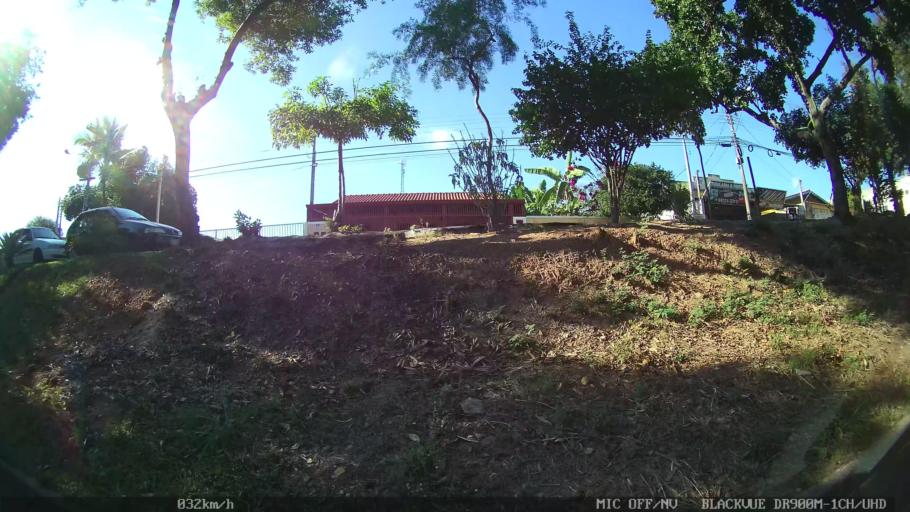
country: BR
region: Sao Paulo
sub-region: Campinas
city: Campinas
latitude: -22.9653
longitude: -47.1084
